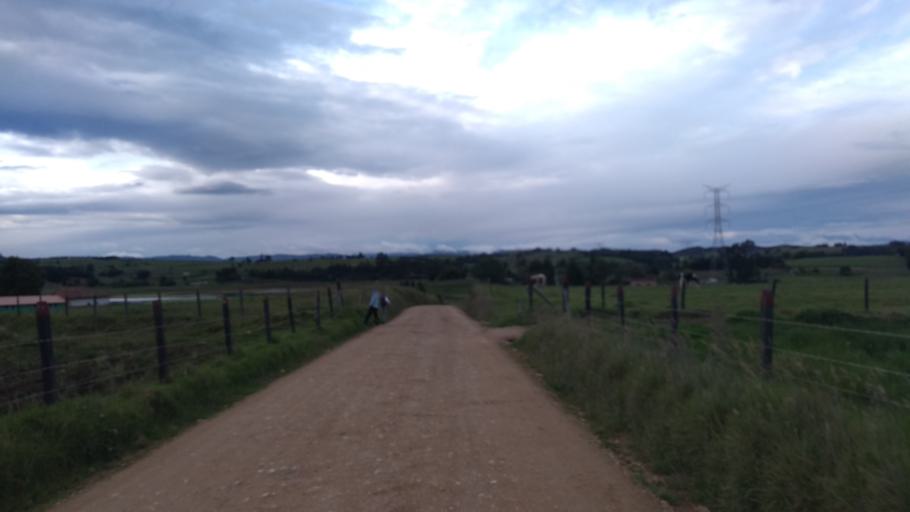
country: CO
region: Boyaca
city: Toca
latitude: 5.6118
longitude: -73.1747
